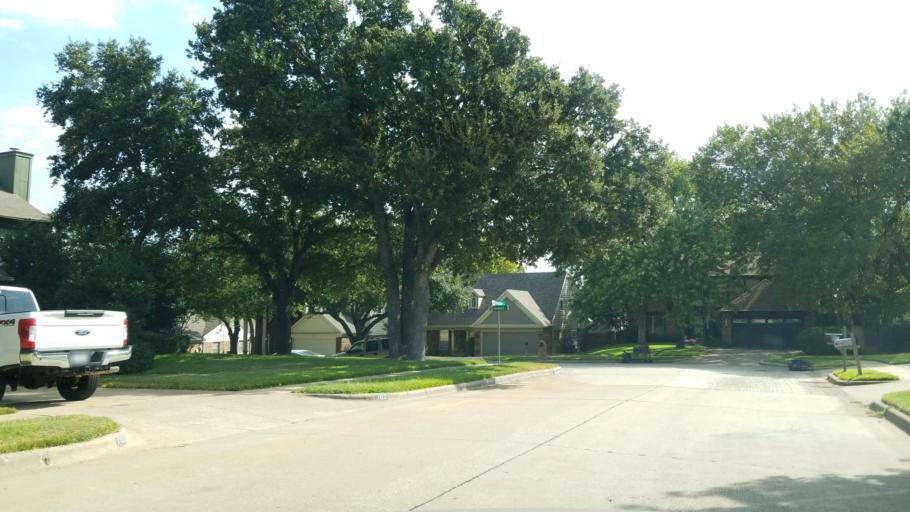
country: US
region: Texas
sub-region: Tarrant County
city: Grapevine
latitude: 32.8901
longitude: -97.0846
